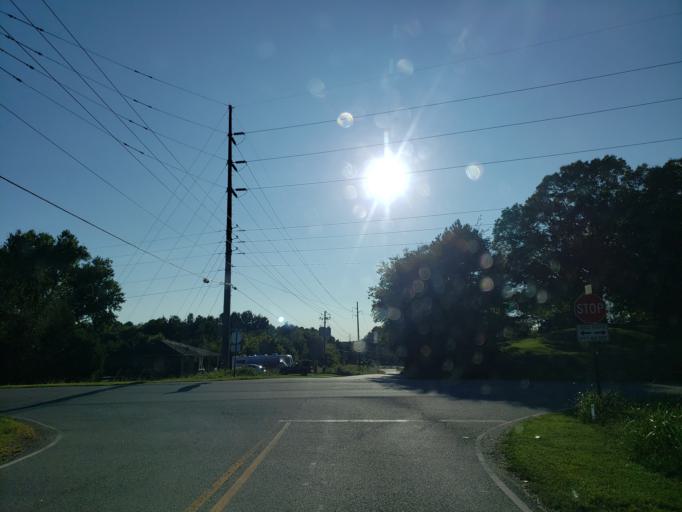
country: US
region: Georgia
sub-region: Bartow County
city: Rydal
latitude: 34.2792
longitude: -84.8111
